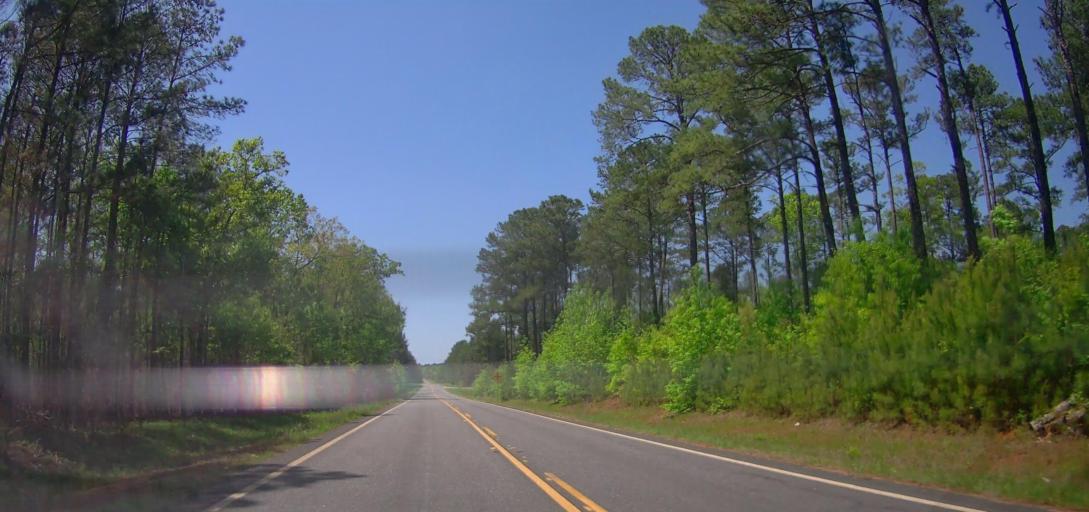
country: US
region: Georgia
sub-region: Putnam County
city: Eatonton
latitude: 33.2265
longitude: -83.5104
